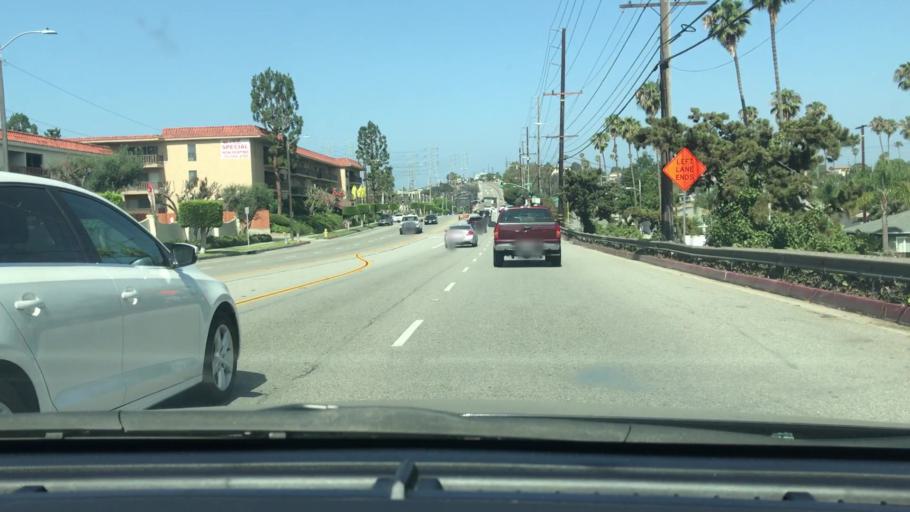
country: US
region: California
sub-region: Los Angeles County
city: Redondo Beach
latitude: 33.8583
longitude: -118.3709
